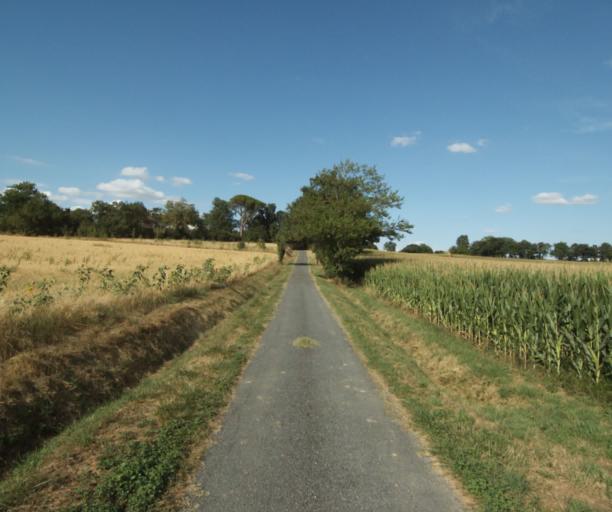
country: FR
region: Midi-Pyrenees
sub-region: Departement du Tarn
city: Puylaurens
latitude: 43.5246
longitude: 1.9859
